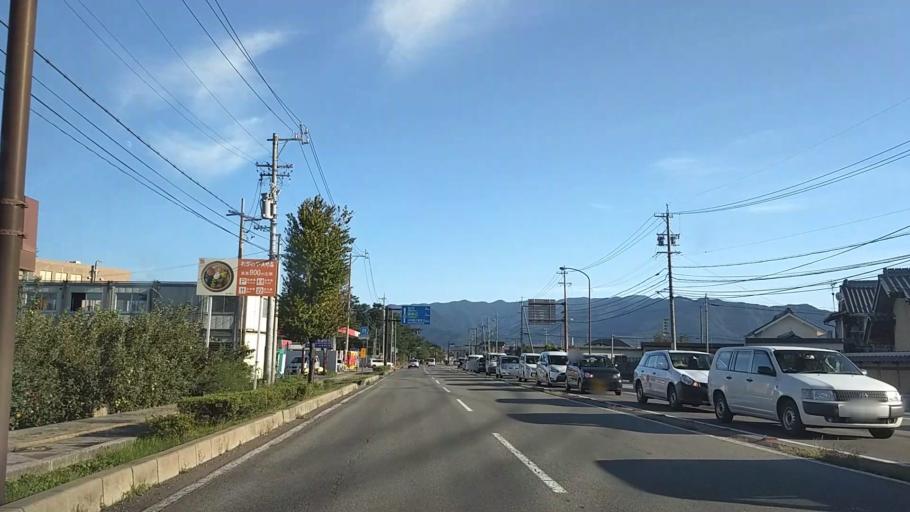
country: JP
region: Nagano
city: Nagano-shi
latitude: 36.5931
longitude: 138.1848
